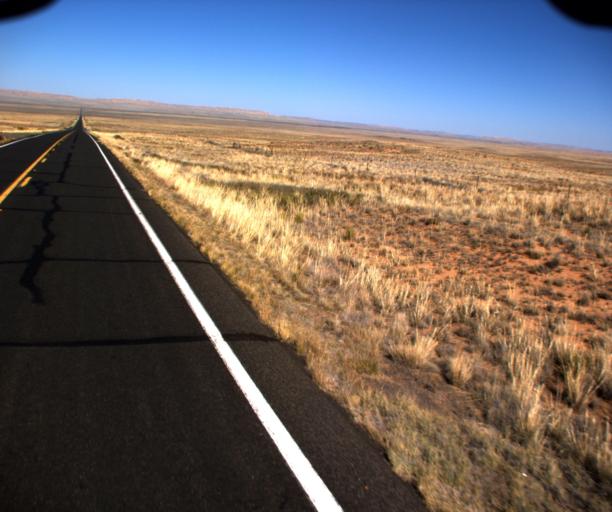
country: US
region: Arizona
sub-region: Navajo County
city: First Mesa
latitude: 35.6420
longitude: -110.4861
